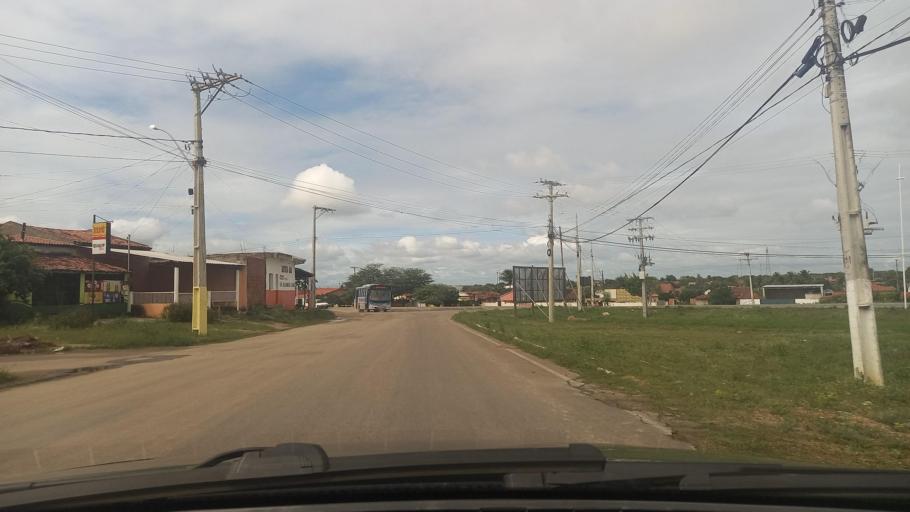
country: BR
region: Bahia
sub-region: Paulo Afonso
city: Paulo Afonso
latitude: -9.4364
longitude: -38.2043
